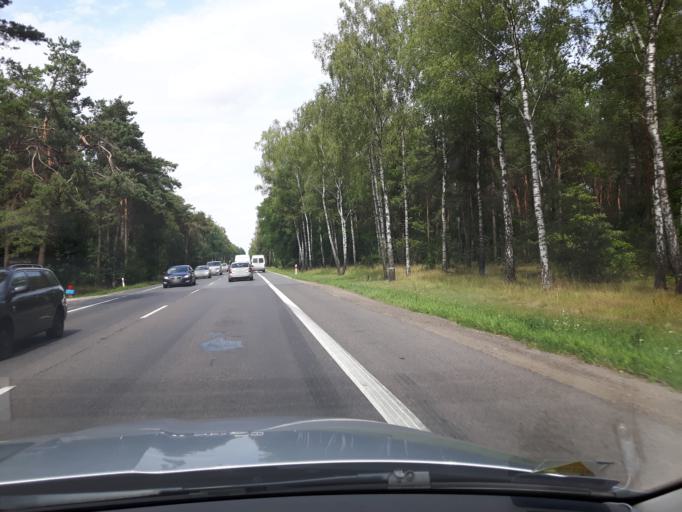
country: PL
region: Masovian Voivodeship
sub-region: Powiat mlawski
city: Strzegowo
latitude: 52.9064
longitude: 20.2868
